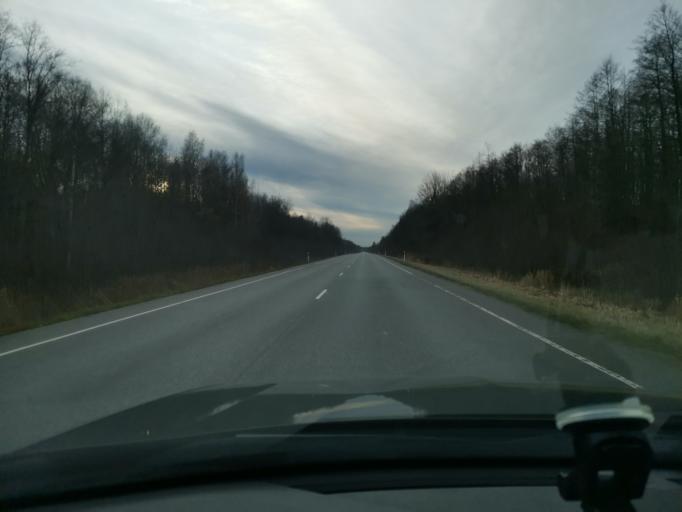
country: EE
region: Ida-Virumaa
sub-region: Narva-Joesuu linn
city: Narva-Joesuu
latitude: 59.3325
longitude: 27.9529
